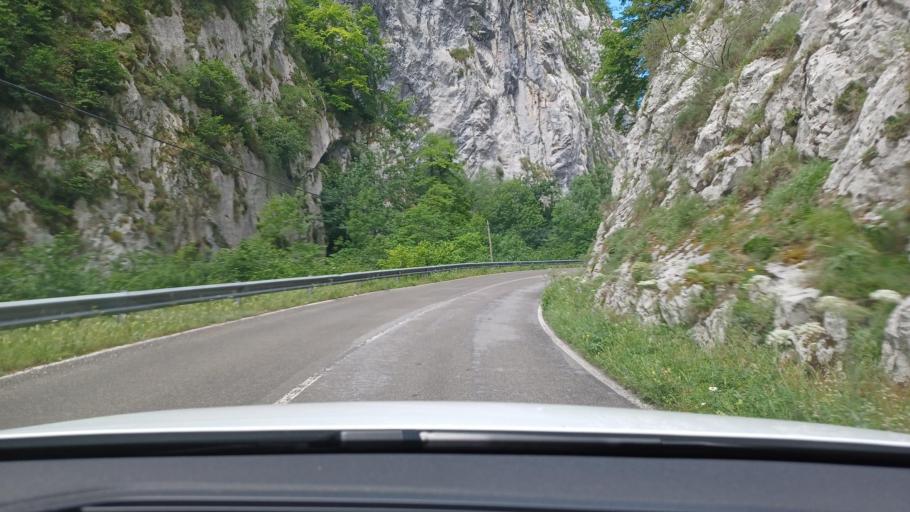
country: ES
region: Asturias
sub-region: Province of Asturias
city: La Plaza
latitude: 43.1218
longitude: -6.0541
